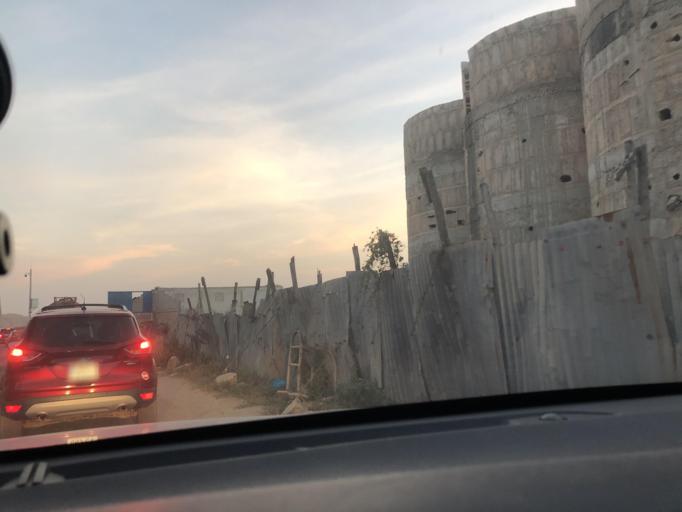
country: SN
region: Dakar
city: Mermoz Boabab
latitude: 14.7365
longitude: -17.5128
